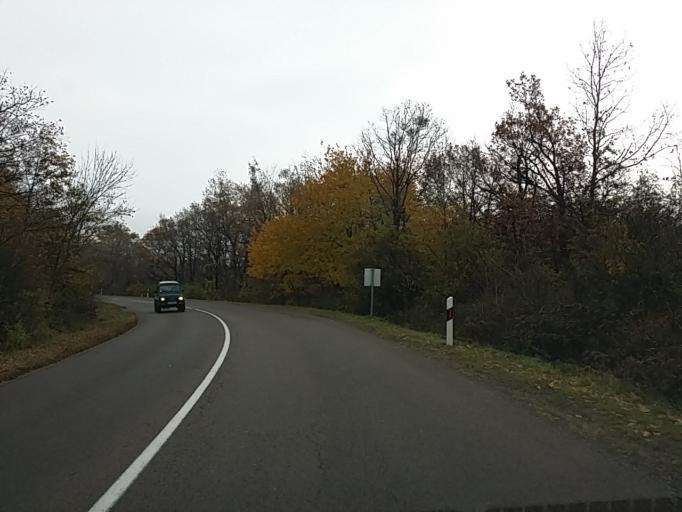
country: HU
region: Heves
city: Gyongyossolymos
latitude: 47.8384
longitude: 19.9566
